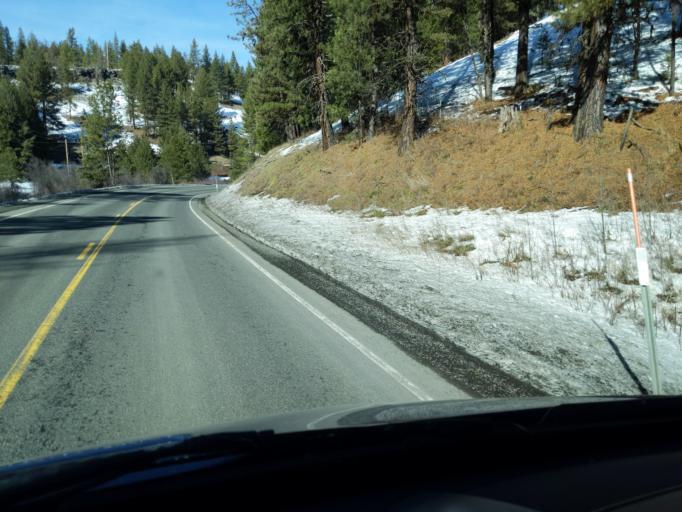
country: US
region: Oregon
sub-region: Grant County
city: John Day
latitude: 44.9335
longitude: -119.0106
